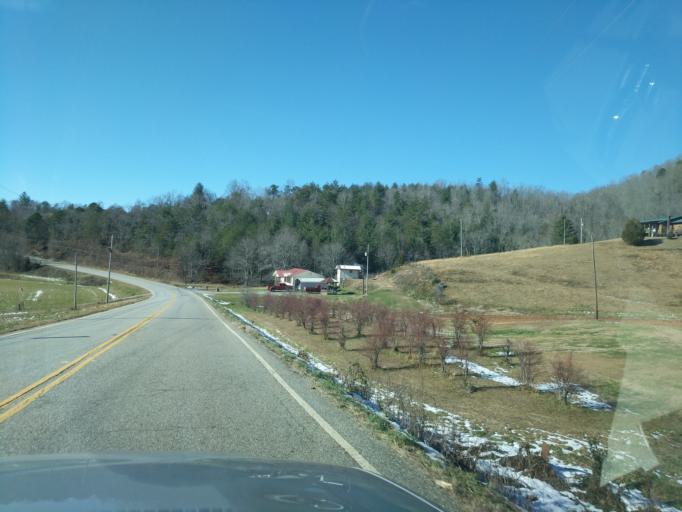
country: US
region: Georgia
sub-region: Towns County
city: Hiawassee
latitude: 34.9305
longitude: -83.6519
